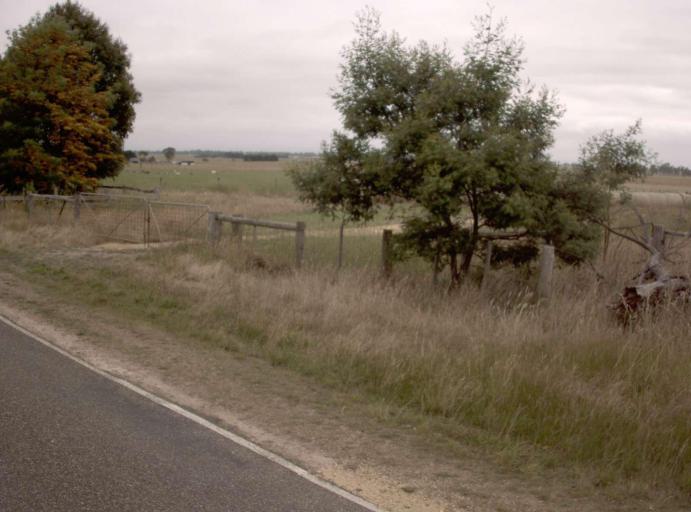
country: AU
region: Victoria
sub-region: Wellington
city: Heyfield
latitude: -38.1131
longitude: 146.7733
